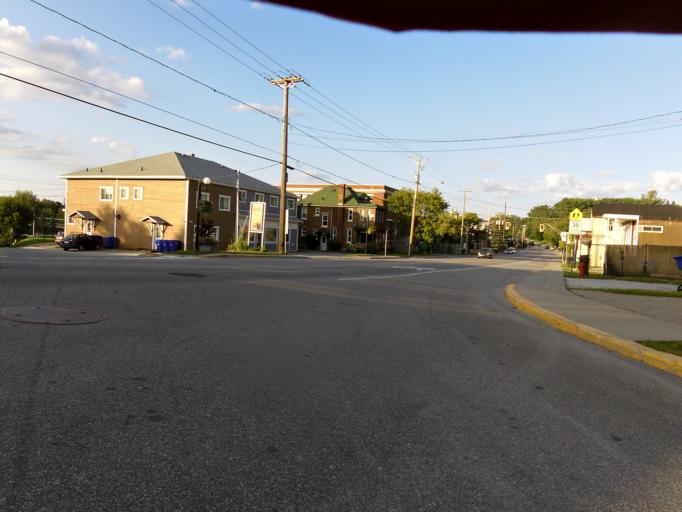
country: CA
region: Quebec
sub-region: Outaouais
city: Maniwaki
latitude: 46.3769
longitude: -75.9766
